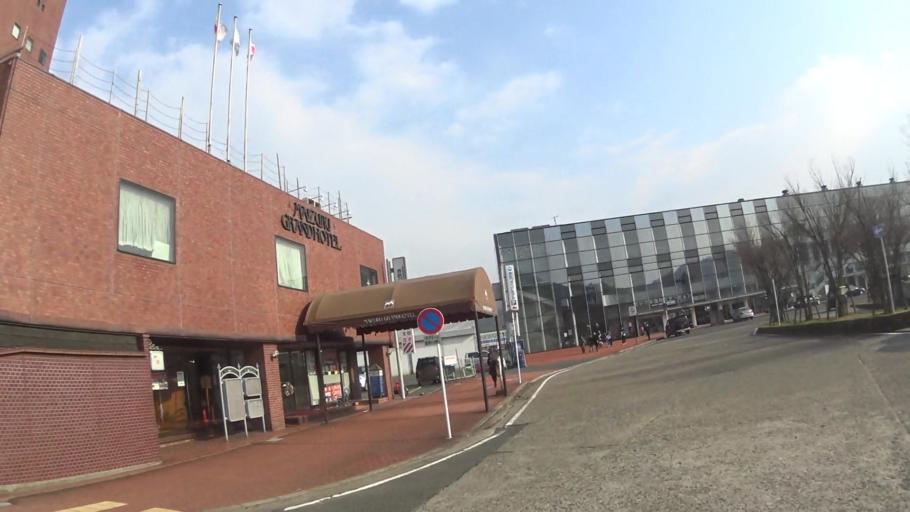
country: JP
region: Kyoto
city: Maizuru
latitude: 35.4420
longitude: 135.3297
